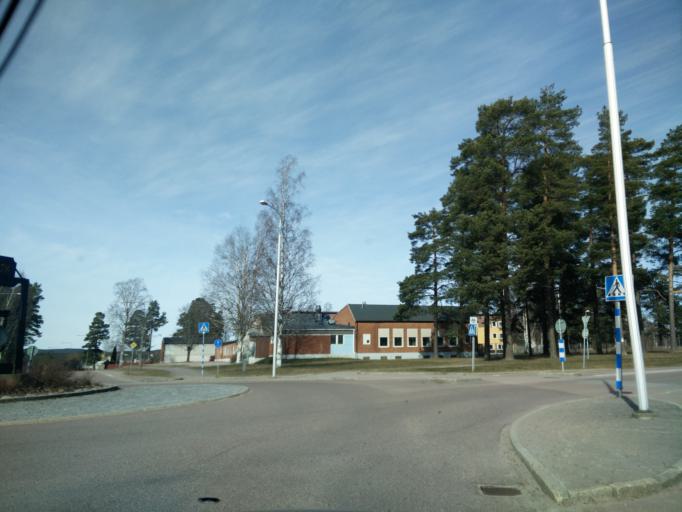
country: SE
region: Vaermland
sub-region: Hagfors Kommun
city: Hagfors
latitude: 60.0404
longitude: 13.6906
